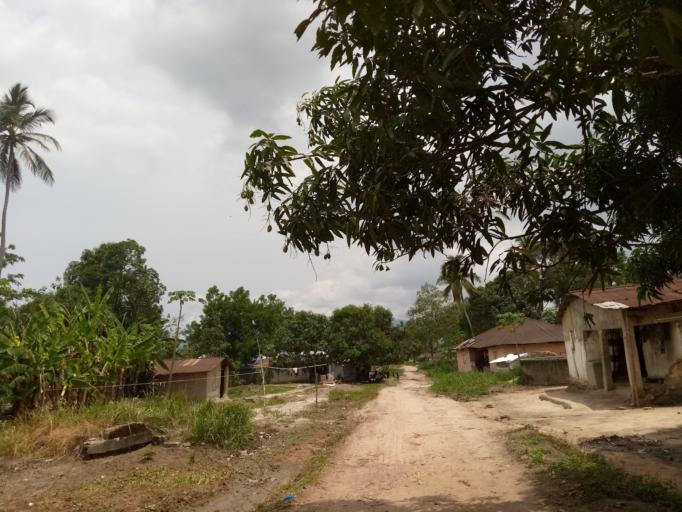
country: SL
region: Western Area
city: Waterloo
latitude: 8.3205
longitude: -13.0328
